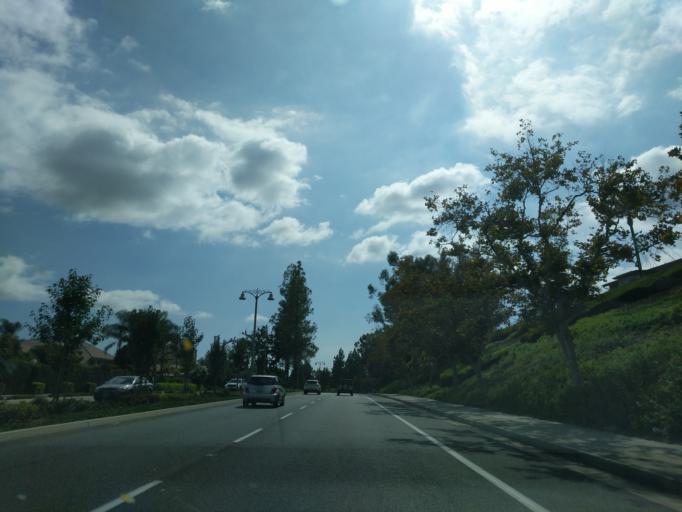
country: US
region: California
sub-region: Orange County
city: Mission Viejo
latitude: 33.6323
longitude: -117.6489
